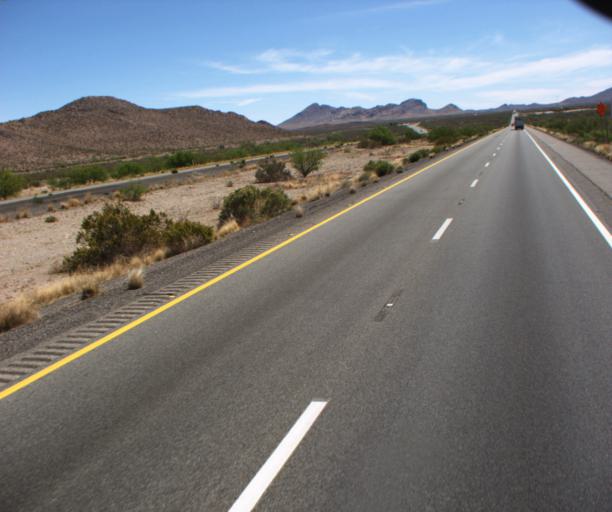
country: US
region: New Mexico
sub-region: Hidalgo County
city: Lordsburg
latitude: 32.2401
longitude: -109.1041
